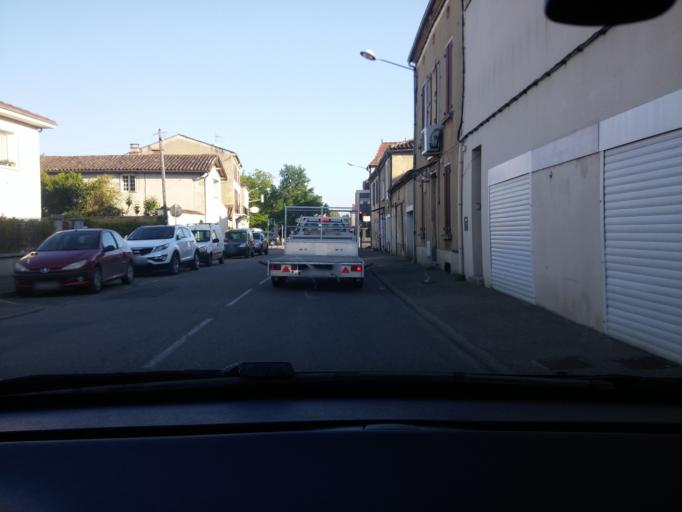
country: FR
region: Aquitaine
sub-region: Departement du Lot-et-Garonne
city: Nerac
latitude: 44.1336
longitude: 0.3455
